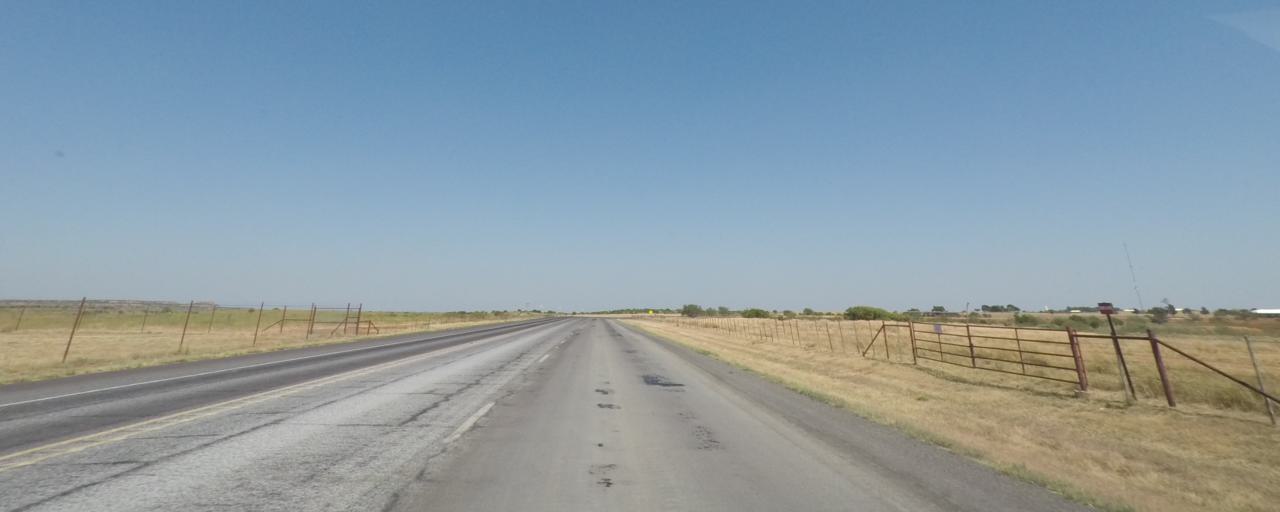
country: US
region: Texas
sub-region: King County
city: Guthrie
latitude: 33.6334
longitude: -100.3479
